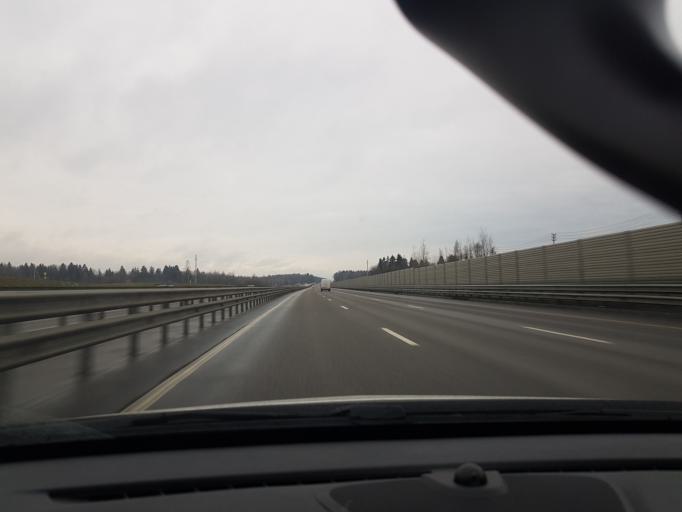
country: RU
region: Moskovskaya
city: Rumyantsevo
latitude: 55.9346
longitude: 36.5539
